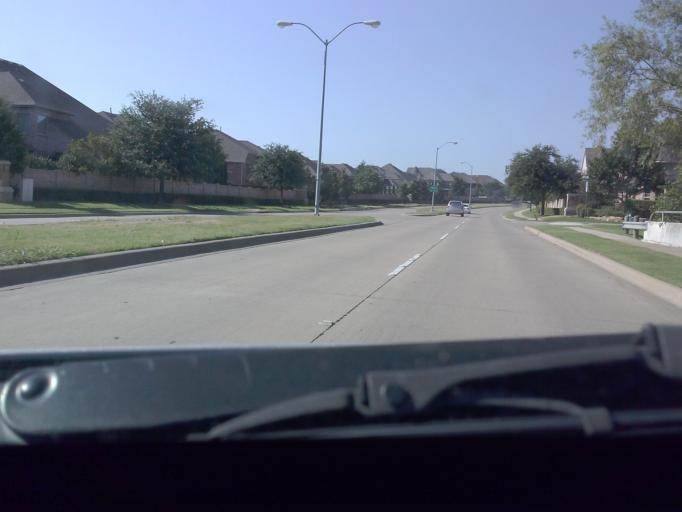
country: US
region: Texas
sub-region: Dallas County
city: Addison
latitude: 33.0393
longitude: -96.7895
